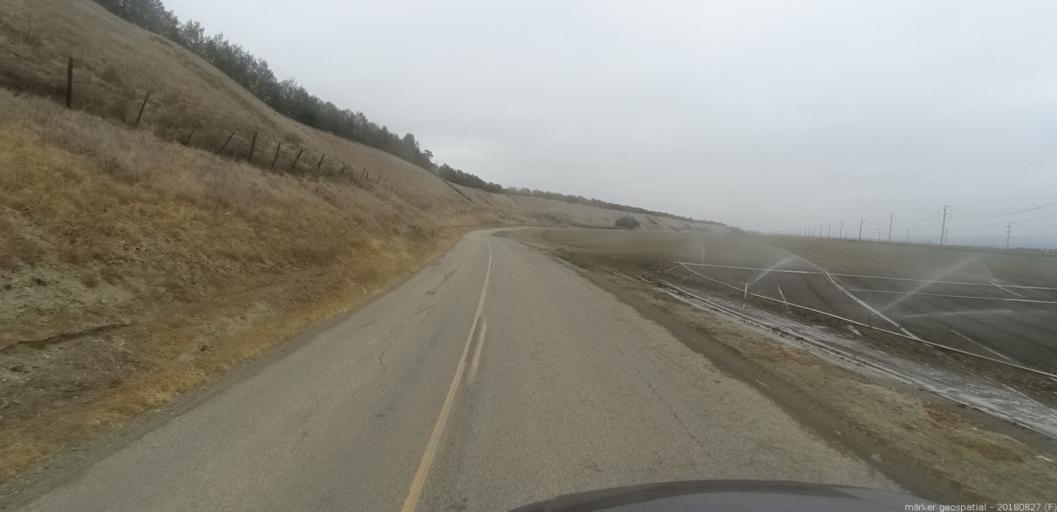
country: US
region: California
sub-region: Monterey County
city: King City
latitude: 36.2602
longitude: -121.1413
